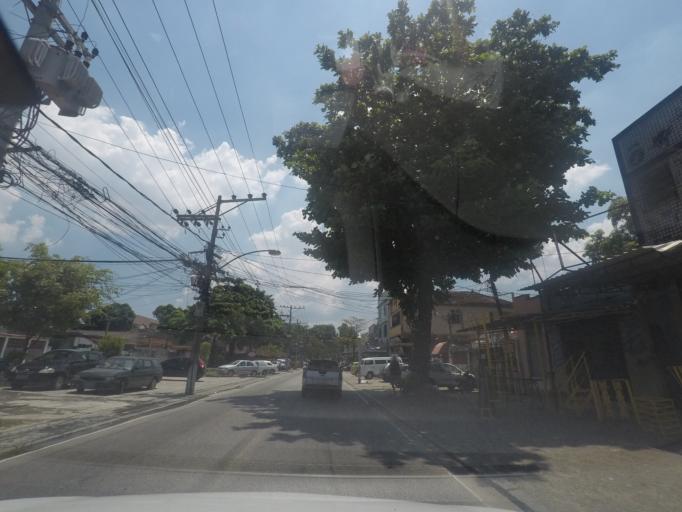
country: BR
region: Rio de Janeiro
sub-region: Duque De Caxias
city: Duque de Caxias
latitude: -22.8243
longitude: -43.3107
